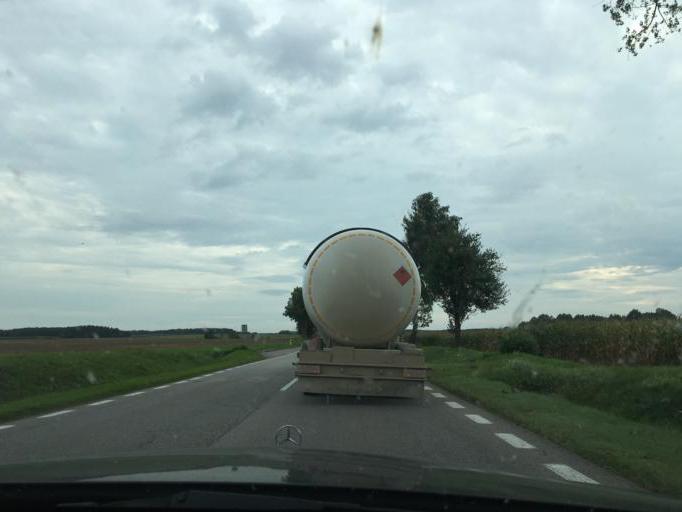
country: PL
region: Podlasie
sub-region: Powiat kolnenski
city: Stawiski
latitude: 53.3067
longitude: 22.1489
